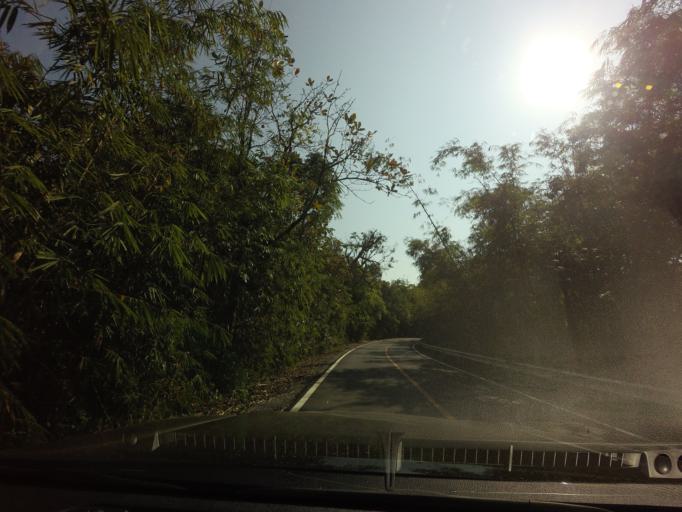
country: TH
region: Kanchanaburi
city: Thong Pha Phum
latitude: 14.6898
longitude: 98.4101
